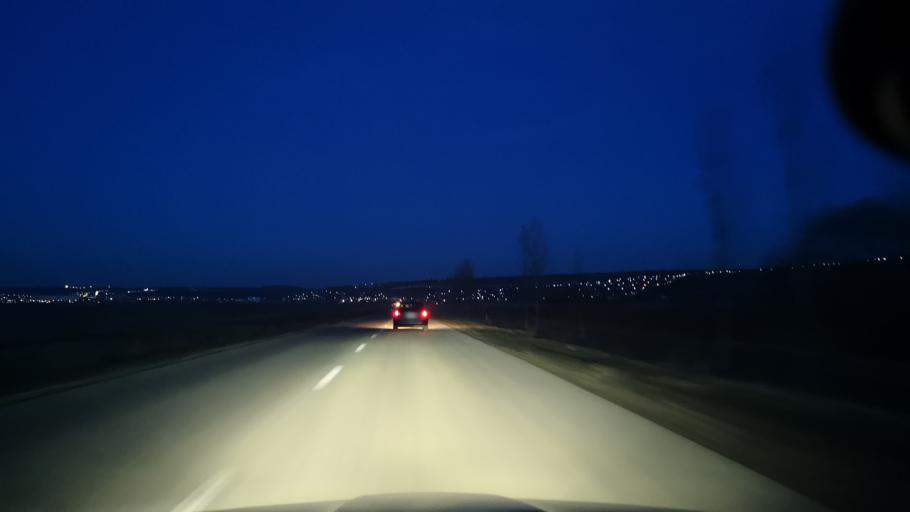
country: MD
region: Orhei
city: Orhei
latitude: 47.3443
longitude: 28.7820
